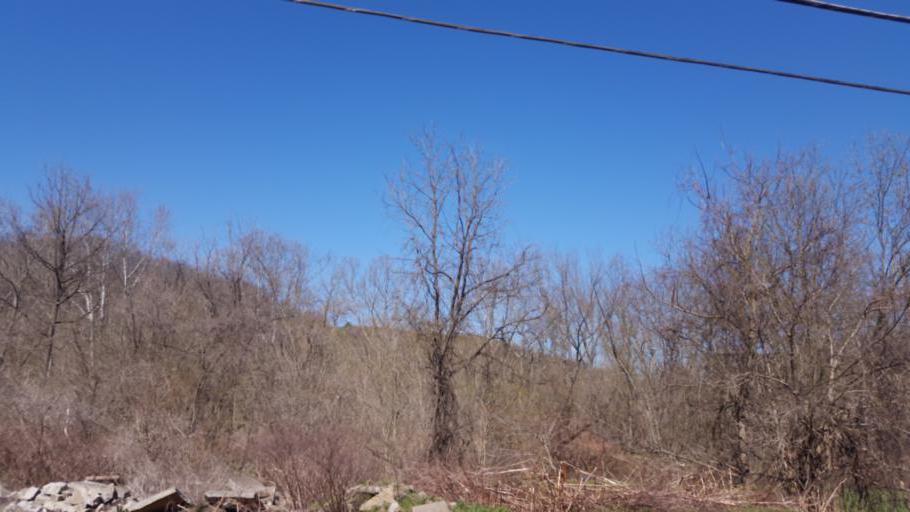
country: US
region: Ohio
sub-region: Jefferson County
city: Tiltonsville
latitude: 40.1836
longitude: -80.6993
